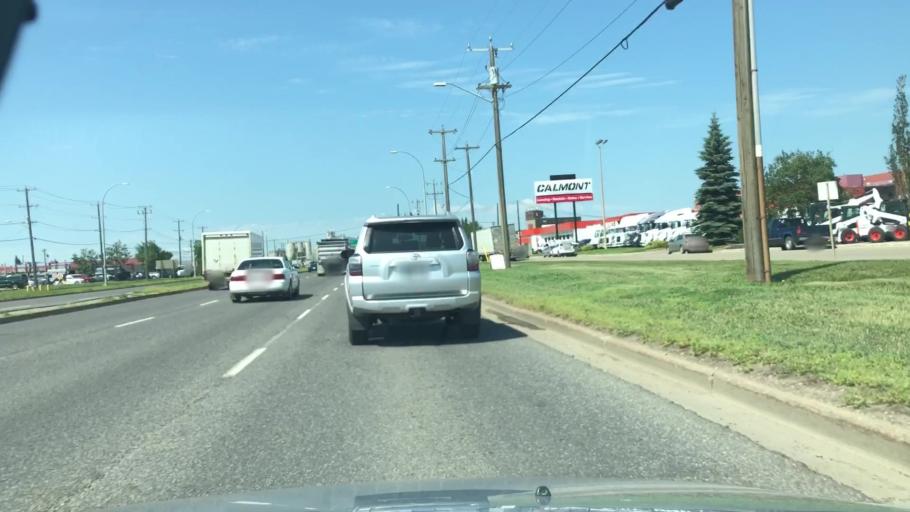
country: CA
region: Alberta
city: St. Albert
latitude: 53.5815
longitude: -113.5718
